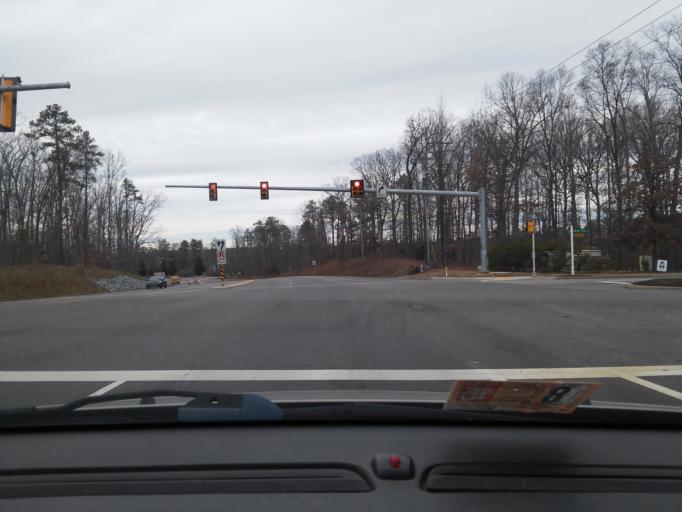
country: US
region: Virginia
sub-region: Chesterfield County
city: Bon Air
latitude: 37.5472
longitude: -77.6529
